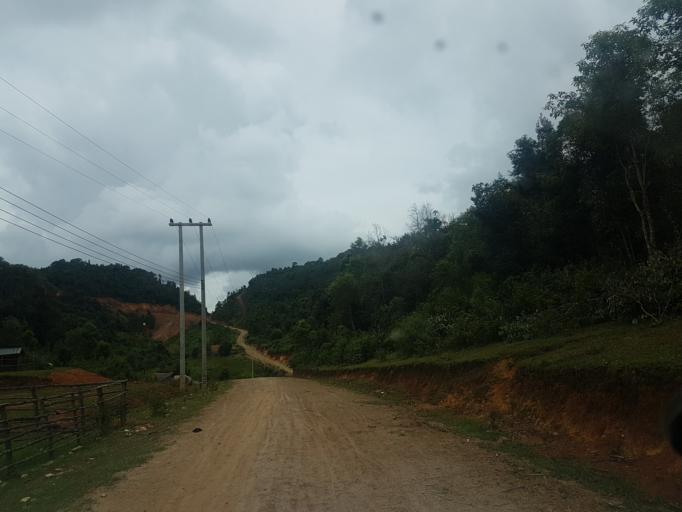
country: LA
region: Xiangkhoang
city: Phonsavan
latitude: 19.3093
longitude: 102.9535
